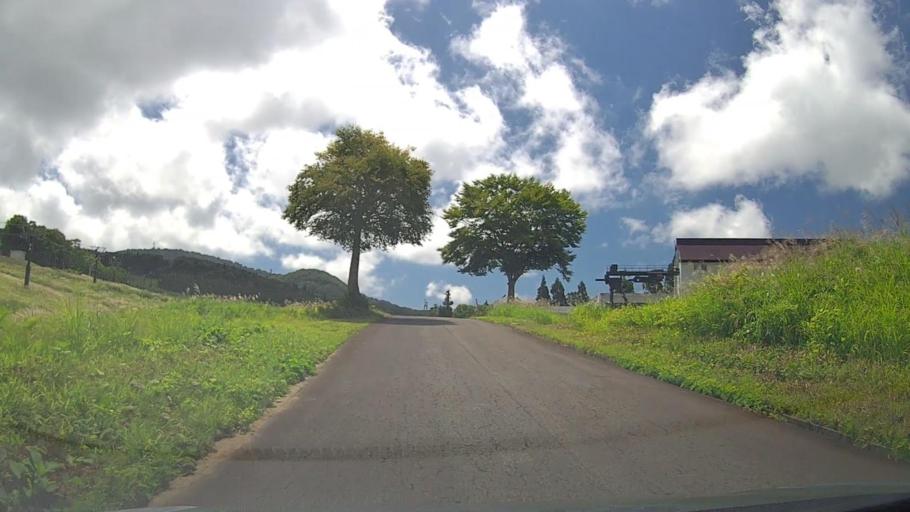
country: JP
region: Nagano
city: Iiyama
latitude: 36.9223
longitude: 138.4777
